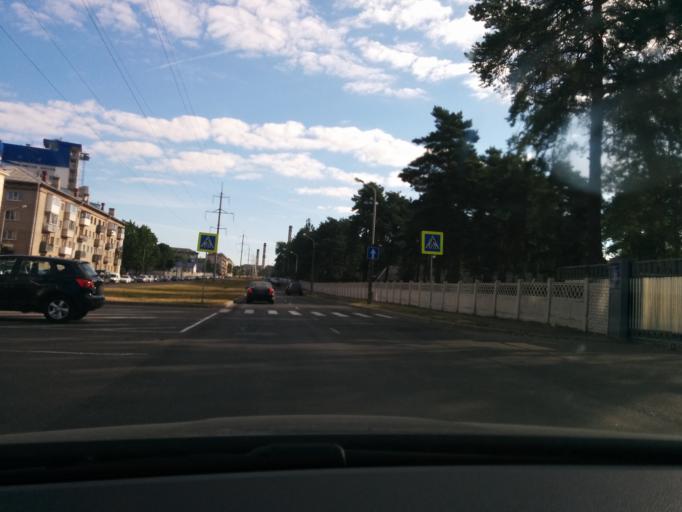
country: BY
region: Minsk
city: Minsk
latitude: 53.8669
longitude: 27.6332
